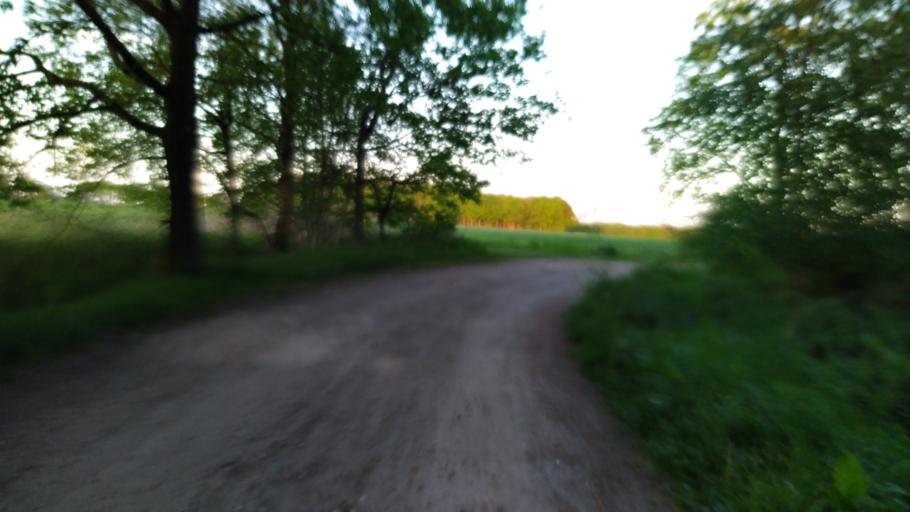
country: DE
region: Lower Saxony
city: Bargstedt
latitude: 53.4877
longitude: 9.4541
